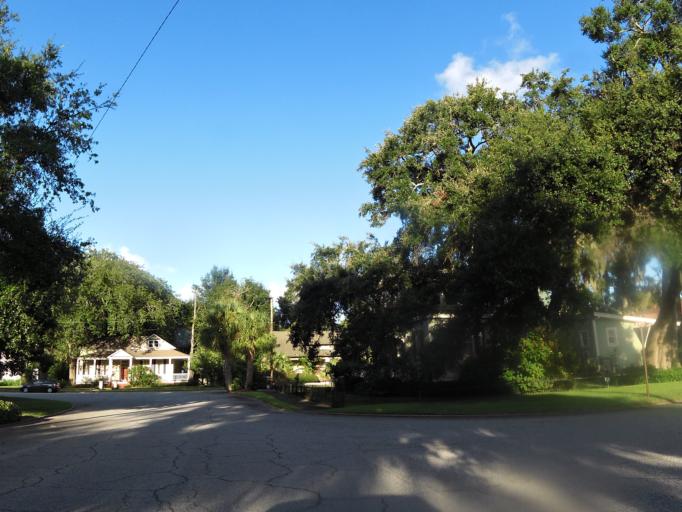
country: US
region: Georgia
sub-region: Glynn County
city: Brunswick
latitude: 31.1428
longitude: -81.4931
